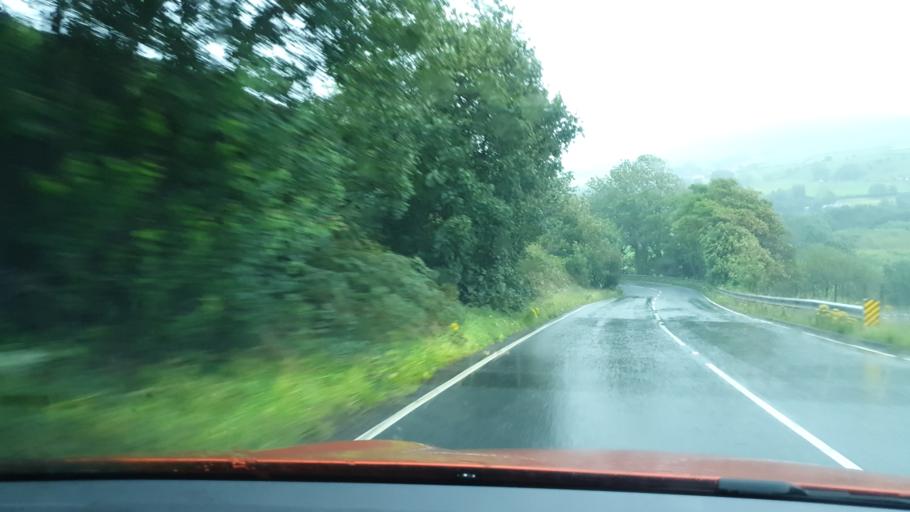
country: GB
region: England
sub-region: Cumbria
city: Askam in Furness
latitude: 54.2566
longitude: -3.1778
